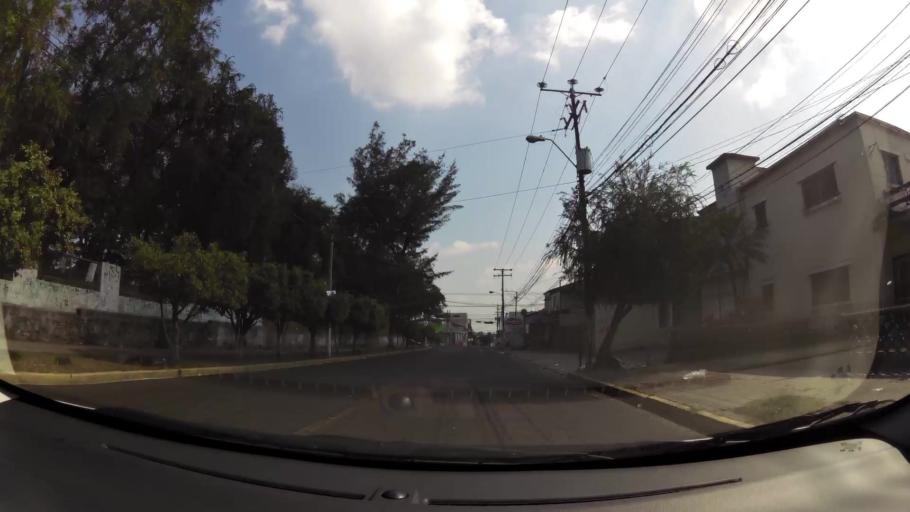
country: SV
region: San Salvador
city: San Salvador
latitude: 13.6977
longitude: -89.2059
